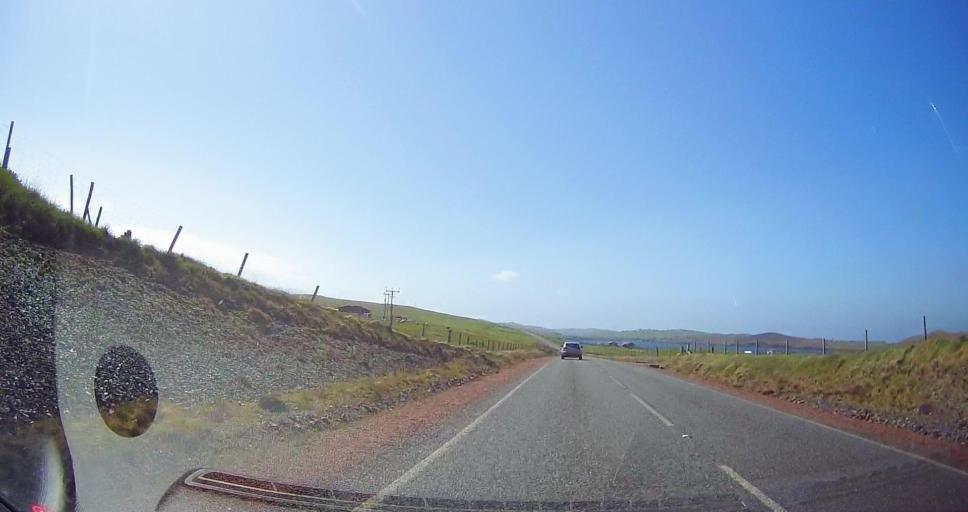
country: GB
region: Scotland
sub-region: Shetland Islands
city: Sandwick
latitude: 60.1212
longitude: -1.2880
